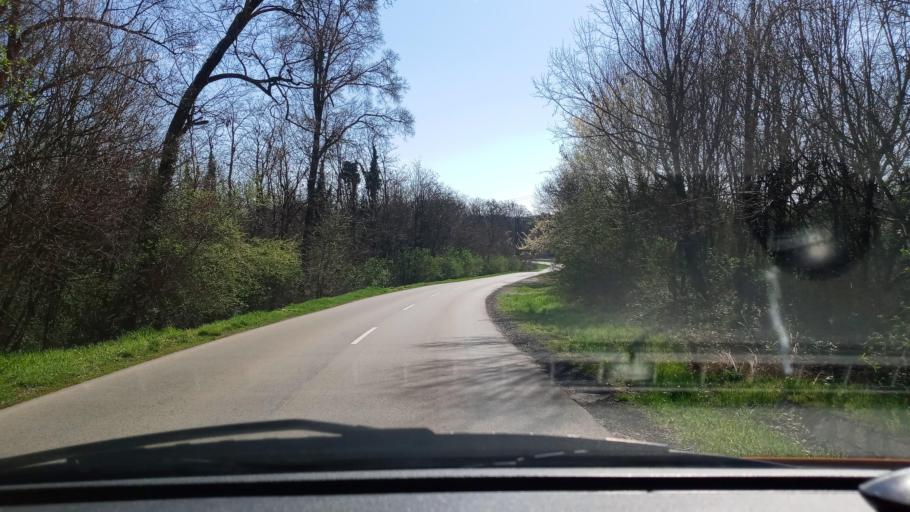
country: HU
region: Baranya
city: Kozarmisleny
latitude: 46.0852
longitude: 18.3032
